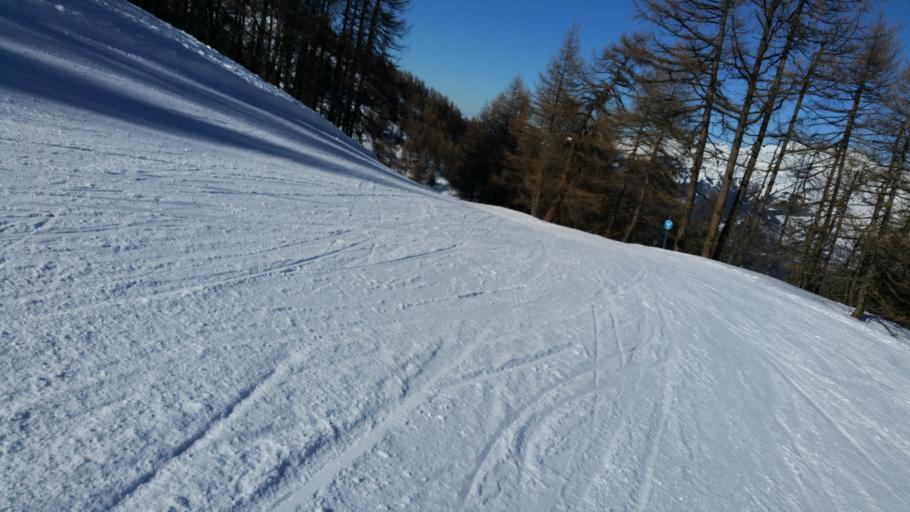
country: FR
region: Rhone-Alpes
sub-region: Departement de la Savoie
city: Villargondran
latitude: 45.2200
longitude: 6.3973
